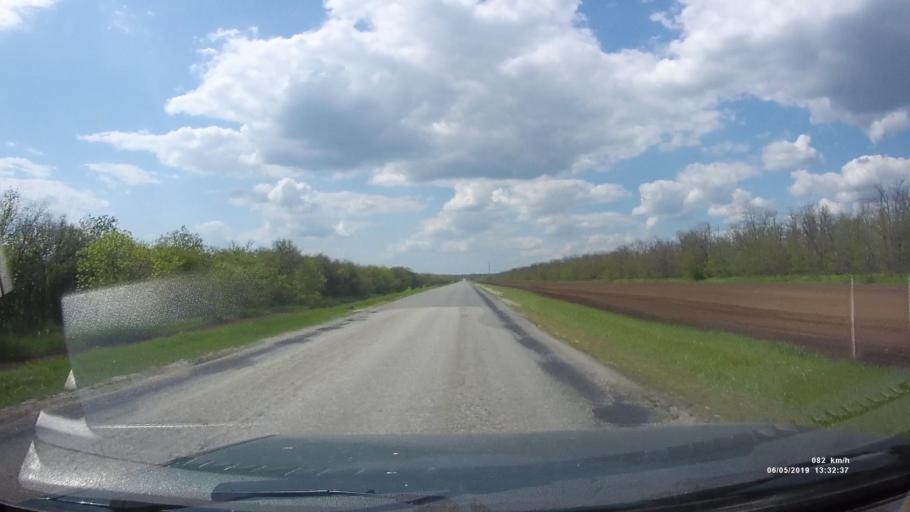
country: RU
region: Rostov
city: Ust'-Donetskiy
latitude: 47.6849
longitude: 40.7928
